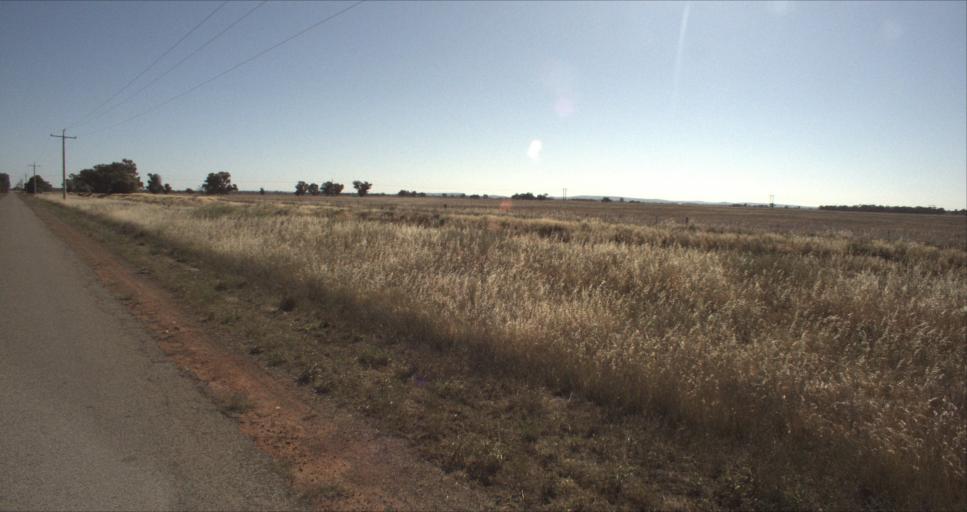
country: AU
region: New South Wales
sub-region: Leeton
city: Leeton
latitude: -34.5798
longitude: 146.3090
